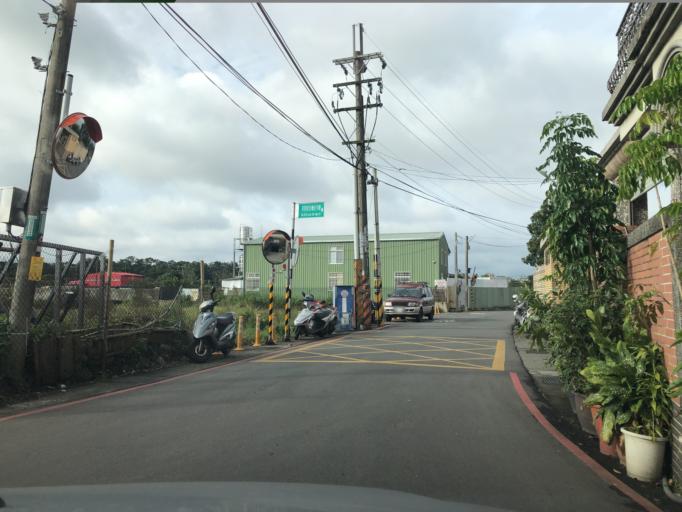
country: TW
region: Taiwan
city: Daxi
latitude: 24.9174
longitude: 121.2592
